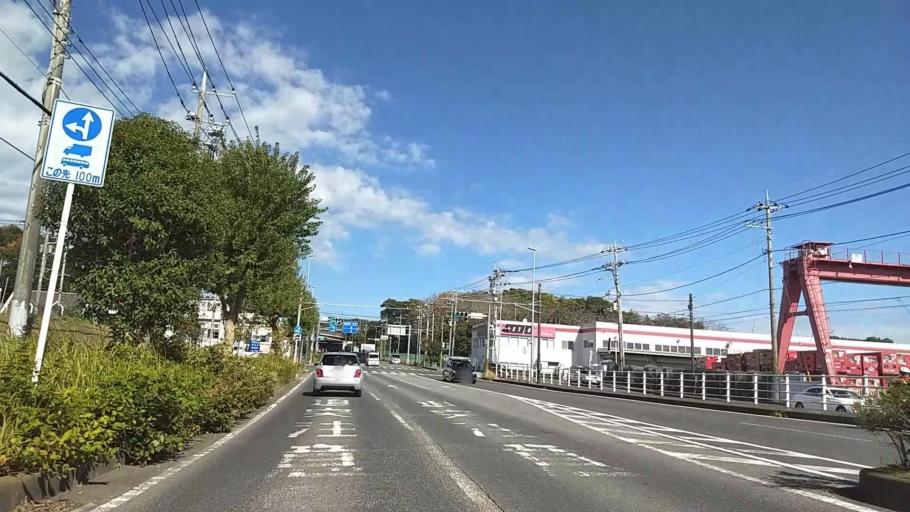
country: JP
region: Kanagawa
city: Hadano
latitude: 35.3498
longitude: 139.2351
